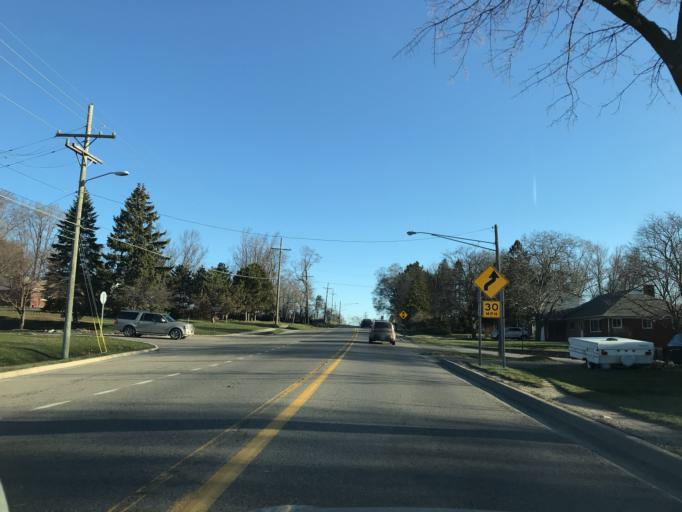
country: US
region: Michigan
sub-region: Oakland County
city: Walled Lake
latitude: 42.5267
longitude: -83.4918
